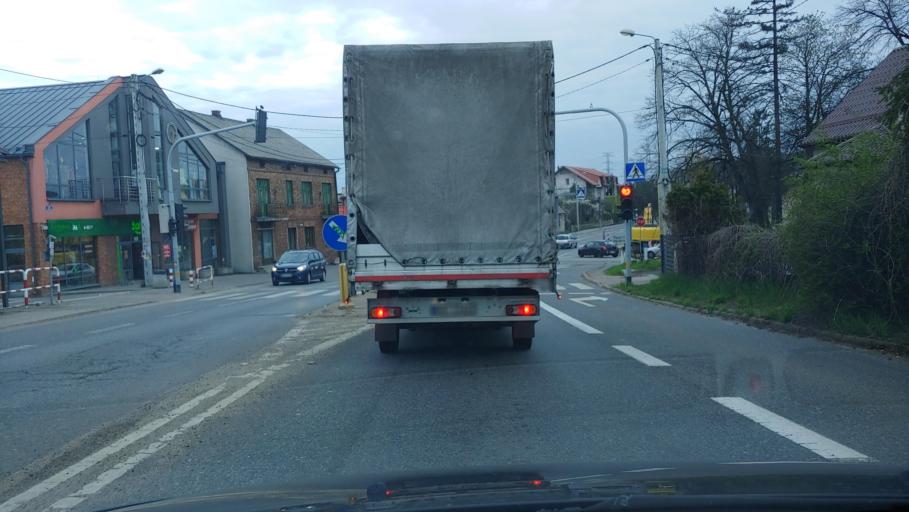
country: PL
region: Silesian Voivodeship
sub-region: Jaworzno
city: Jaworzno
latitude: 50.1634
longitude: 19.3080
